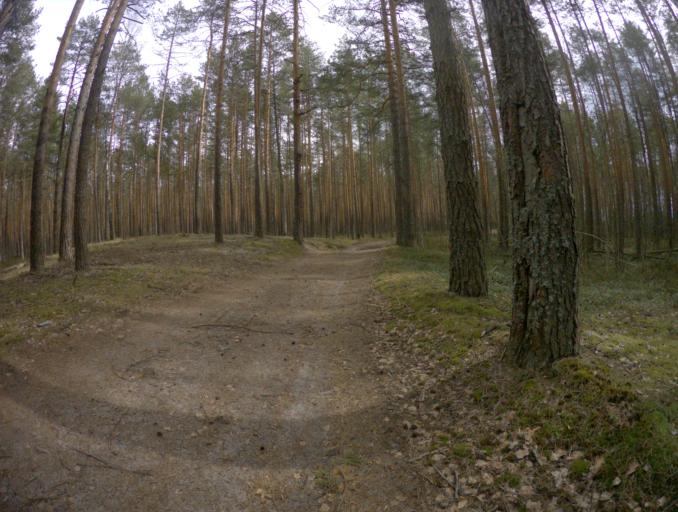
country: RU
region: Vladimir
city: Raduzhnyy
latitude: 55.9470
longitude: 40.2743
